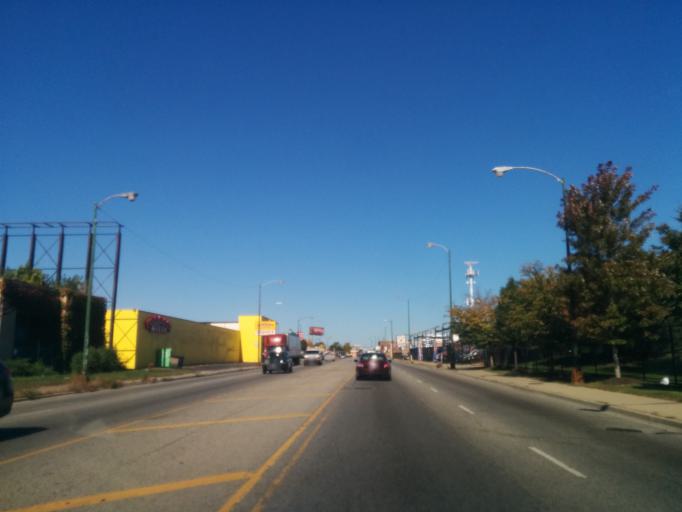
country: US
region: Illinois
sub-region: Cook County
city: Oak Park
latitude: 41.9065
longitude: -87.7460
